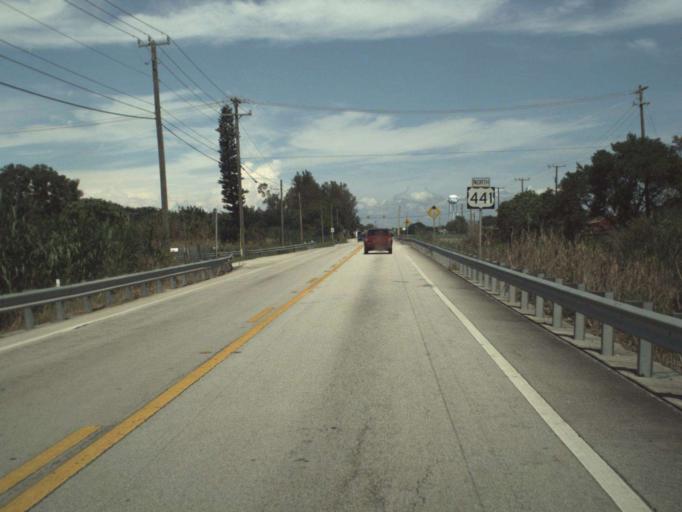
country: US
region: Florida
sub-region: Palm Beach County
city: Pahokee
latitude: 26.8049
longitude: -80.6533
